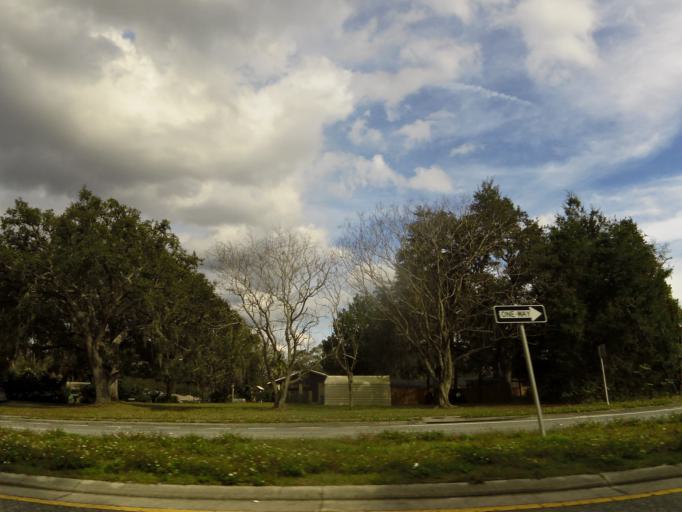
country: US
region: Florida
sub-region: Volusia County
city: North DeLand
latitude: 29.0735
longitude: -81.3255
